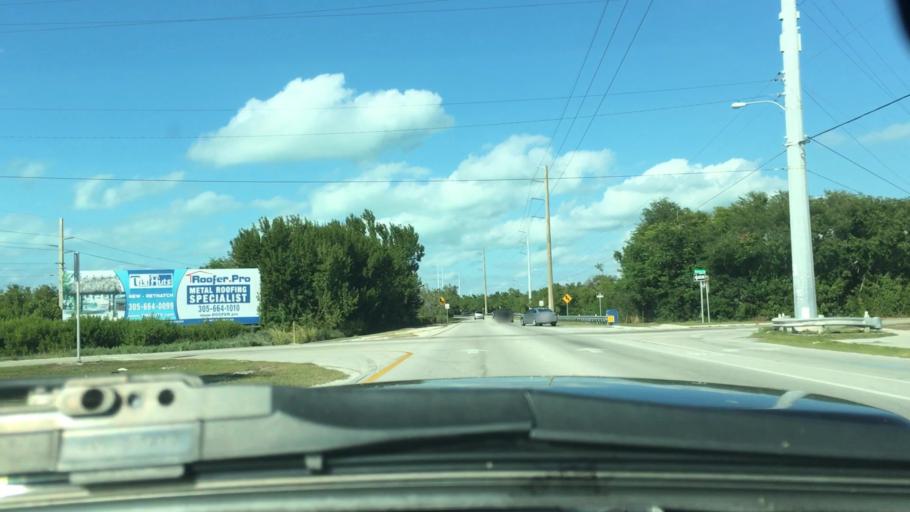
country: US
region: Florida
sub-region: Monroe County
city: Tavernier
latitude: 25.0183
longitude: -80.5111
